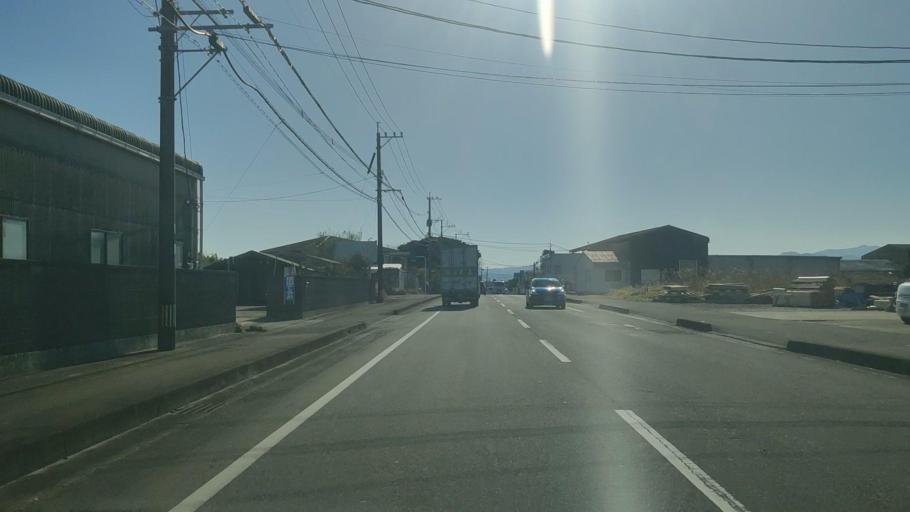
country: JP
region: Miyazaki
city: Miyazaki-shi
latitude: 31.9459
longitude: 131.4589
